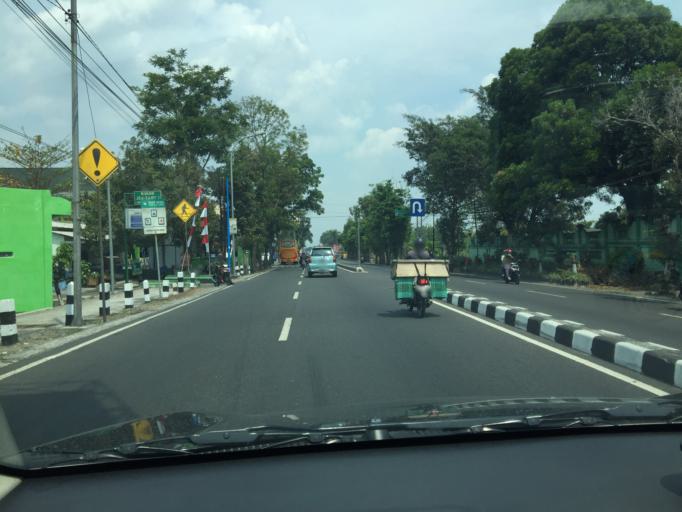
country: ID
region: Daerah Istimewa Yogyakarta
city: Sleman
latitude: -7.6834
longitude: 110.3399
